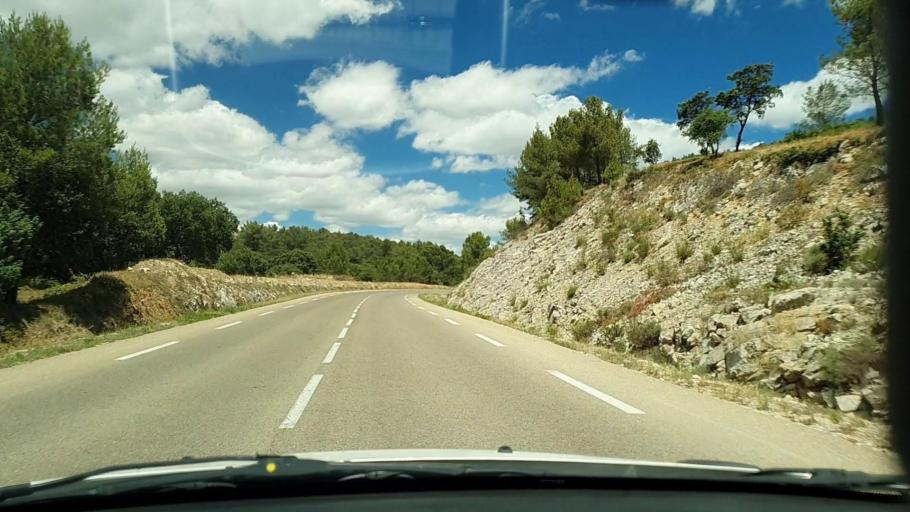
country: FR
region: Languedoc-Roussillon
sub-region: Departement du Gard
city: Poulx
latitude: 43.8877
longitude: 4.4172
